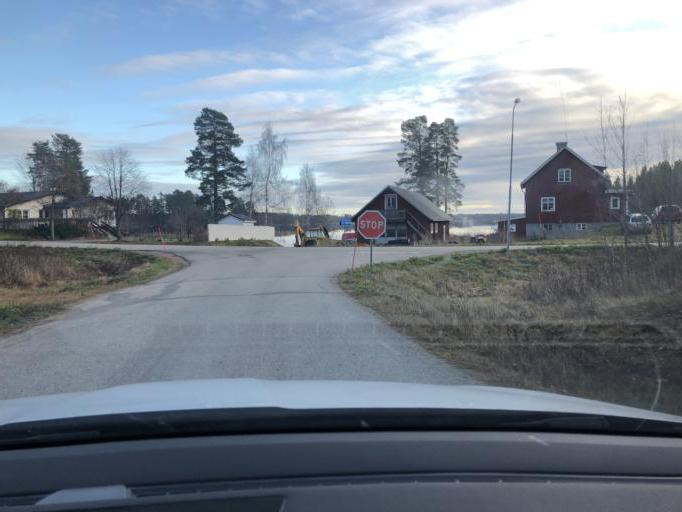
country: SE
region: Gaevleborg
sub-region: Hudiksvalls Kommun
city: Sorforsa
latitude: 61.7102
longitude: 16.9519
